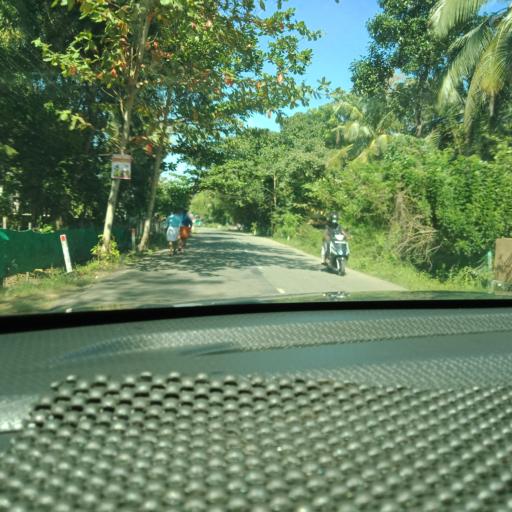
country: IN
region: Kerala
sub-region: Alappuzha
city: Mavelikara
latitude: 9.3121
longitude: 76.4575
